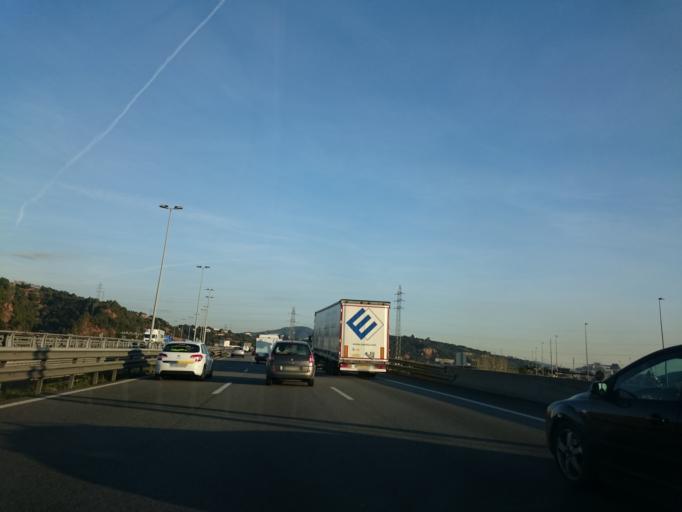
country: ES
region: Catalonia
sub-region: Provincia de Barcelona
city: Castellbisbal
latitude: 41.4699
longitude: 1.9647
